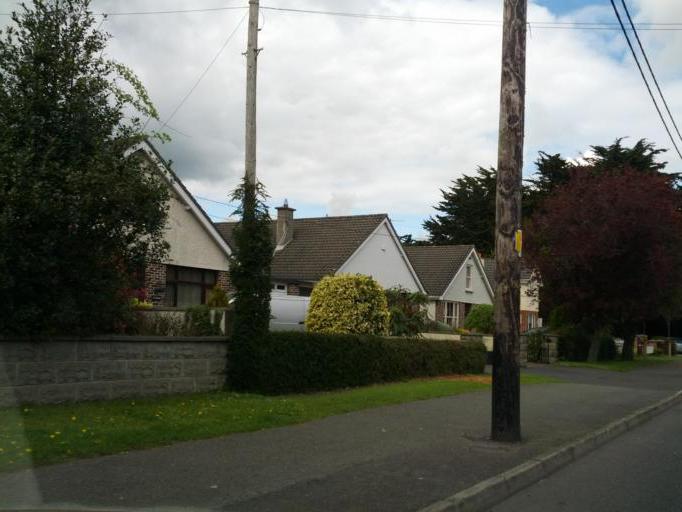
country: IE
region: Leinster
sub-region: Kildare
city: Leixlip
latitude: 53.3635
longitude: -6.4976
